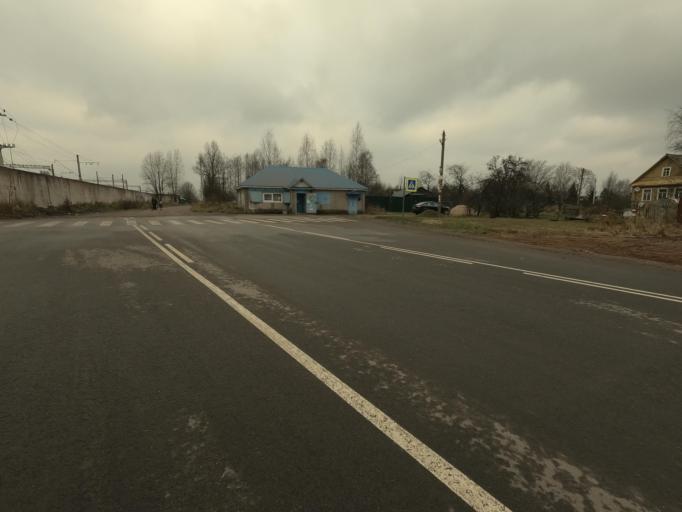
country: RU
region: Leningrad
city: Lyuban'
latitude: 59.4958
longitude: 31.2749
